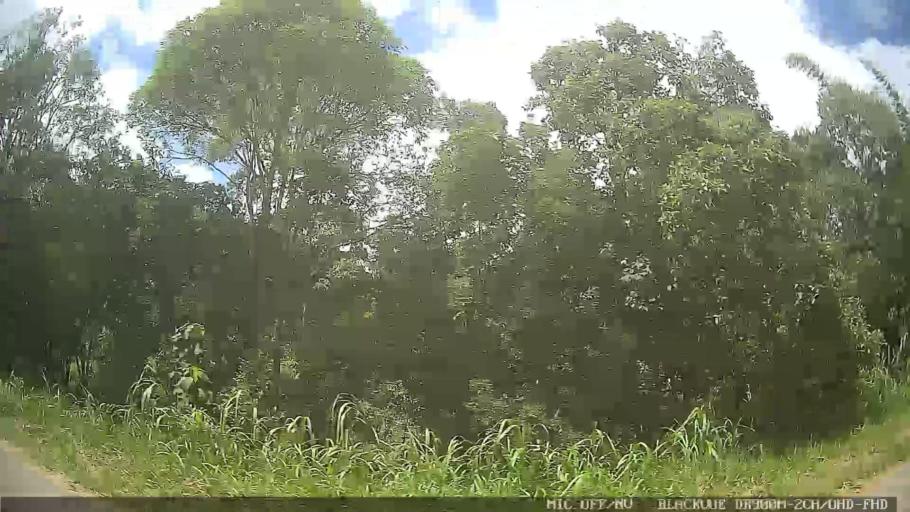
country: BR
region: Sao Paulo
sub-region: Braganca Paulista
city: Braganca Paulista
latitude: -22.8070
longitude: -46.5287
